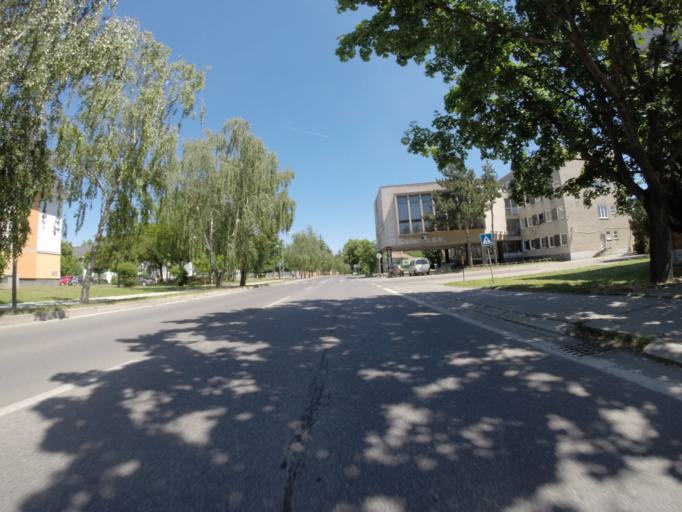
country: SK
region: Trnavsky
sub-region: Okres Galanta
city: Galanta
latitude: 48.1888
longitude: 17.7301
